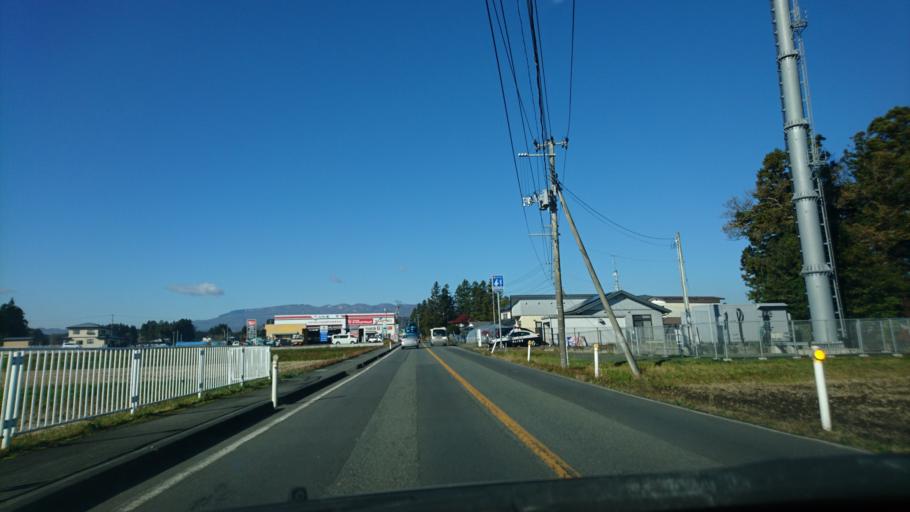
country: JP
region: Iwate
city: Mizusawa
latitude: 39.1291
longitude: 141.0511
